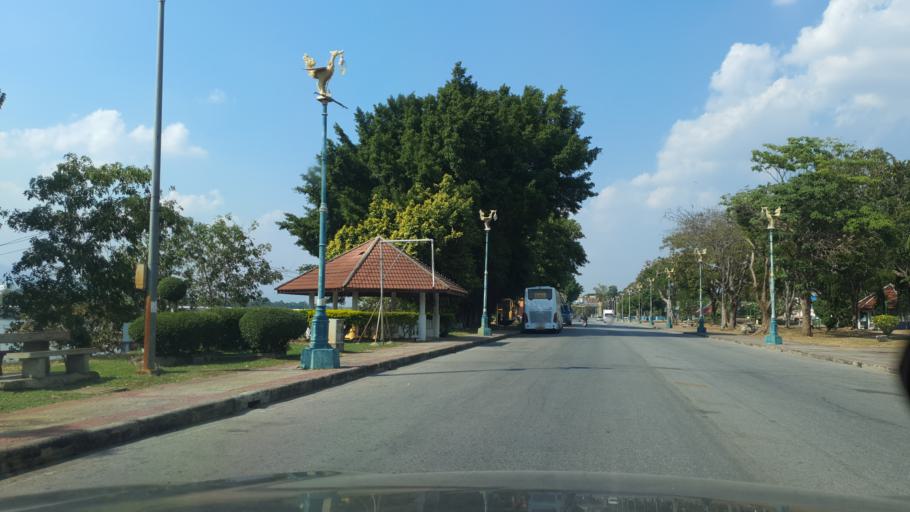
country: TH
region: Tak
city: Tak
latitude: 16.8808
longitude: 99.1195
